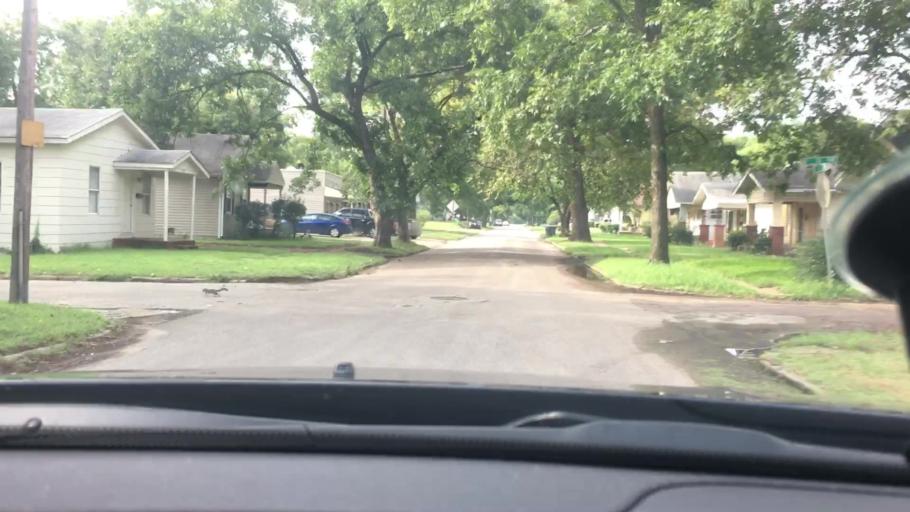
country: US
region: Oklahoma
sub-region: Carter County
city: Ardmore
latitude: 34.1817
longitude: -97.1282
